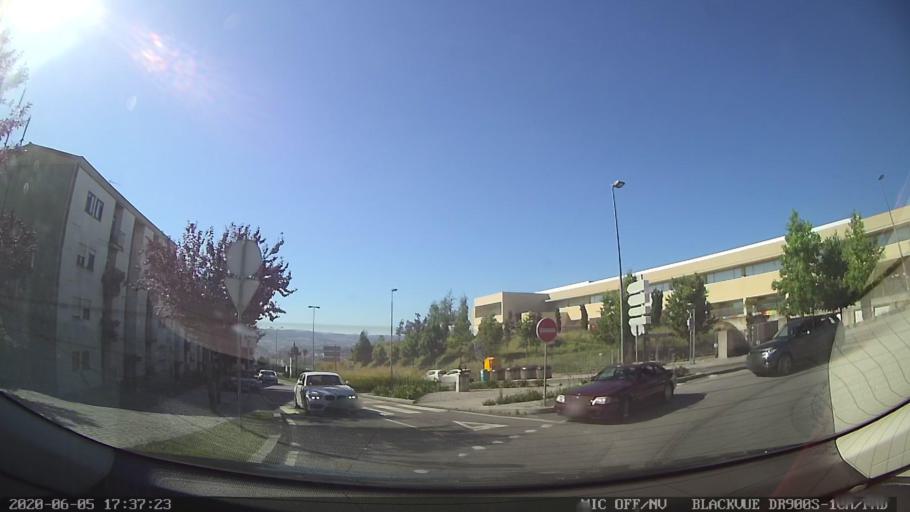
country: PT
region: Porto
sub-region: Penafiel
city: Penafiel
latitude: 41.2080
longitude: -8.2819
